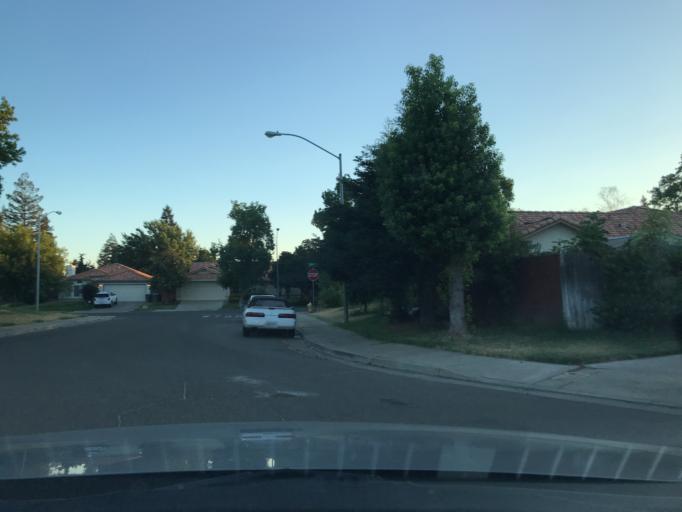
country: US
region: California
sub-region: Merced County
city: Merced
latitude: 37.3120
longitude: -120.5000
